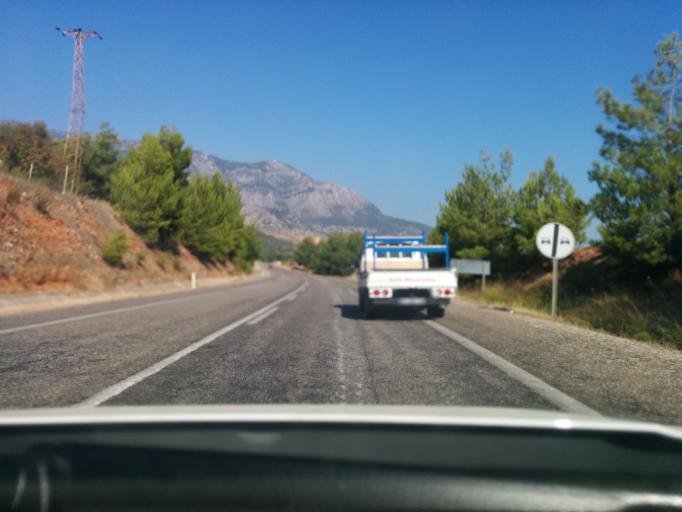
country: TR
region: Mugla
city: Esen
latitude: 36.4276
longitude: 29.2728
